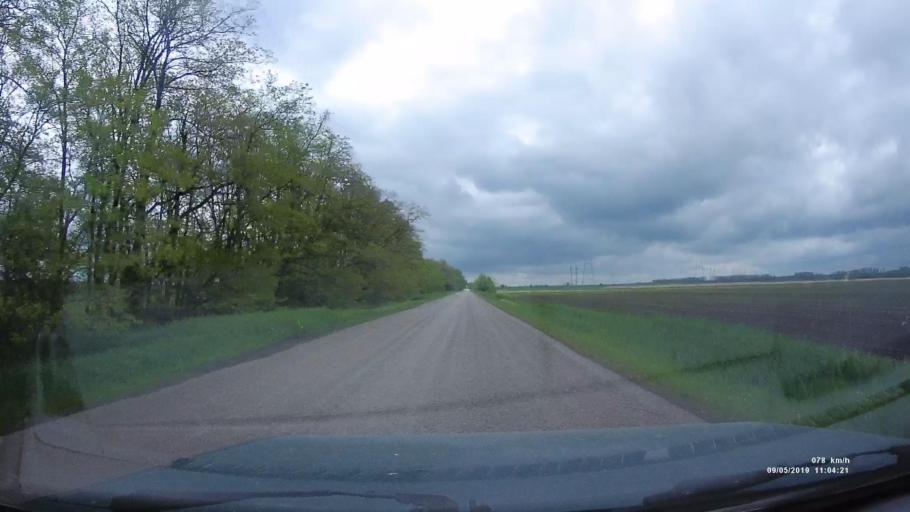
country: RU
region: Krasnodarskiy
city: Kanelovskaya
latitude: 46.8181
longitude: 39.2100
